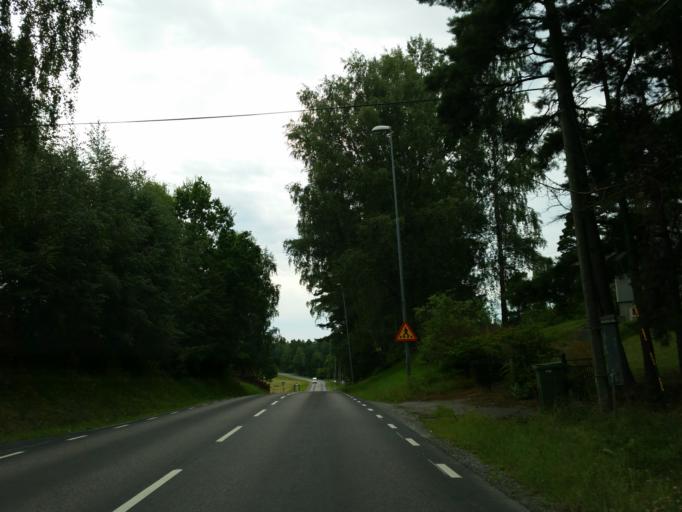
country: SE
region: Stockholm
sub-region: Botkyrka Kommun
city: Eriksberg
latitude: 59.2383
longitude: 17.7823
